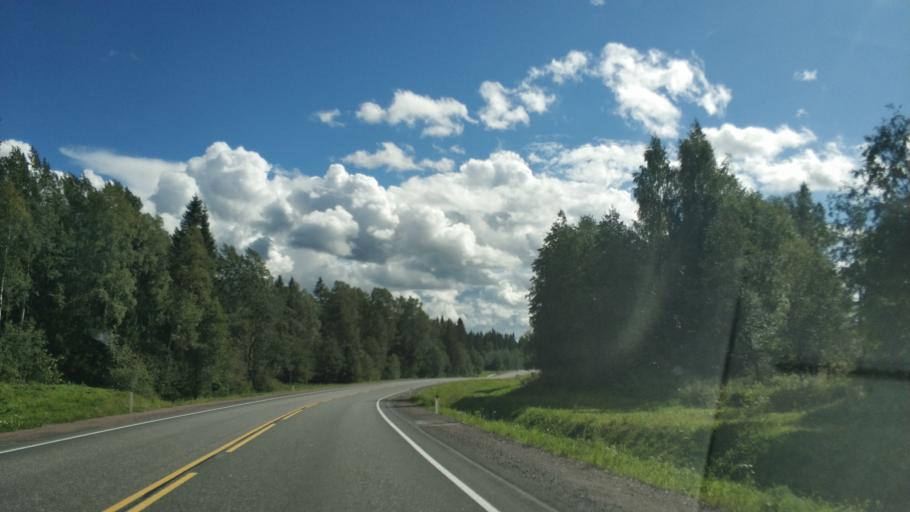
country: RU
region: Republic of Karelia
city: Ruskeala
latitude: 61.8938
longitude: 30.6406
